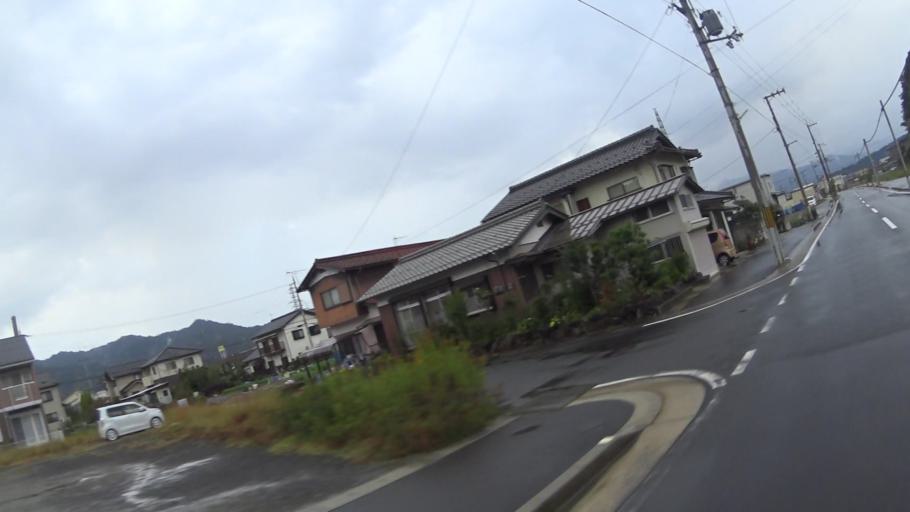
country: JP
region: Kyoto
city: Miyazu
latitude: 35.5347
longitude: 135.2061
